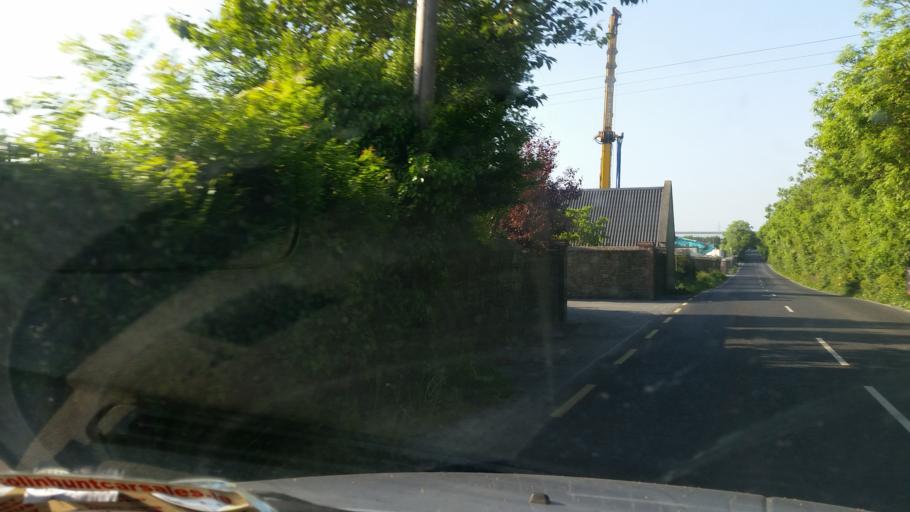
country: IE
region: Leinster
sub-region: Fingal County
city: Blanchardstown
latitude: 53.4137
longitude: -6.3445
